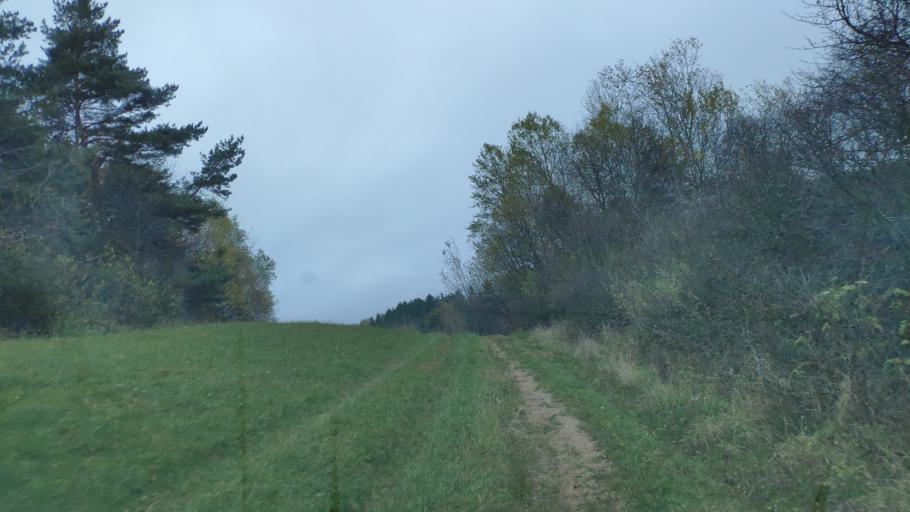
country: SK
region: Presovsky
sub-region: Okres Presov
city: Presov
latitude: 48.9320
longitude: 21.0981
